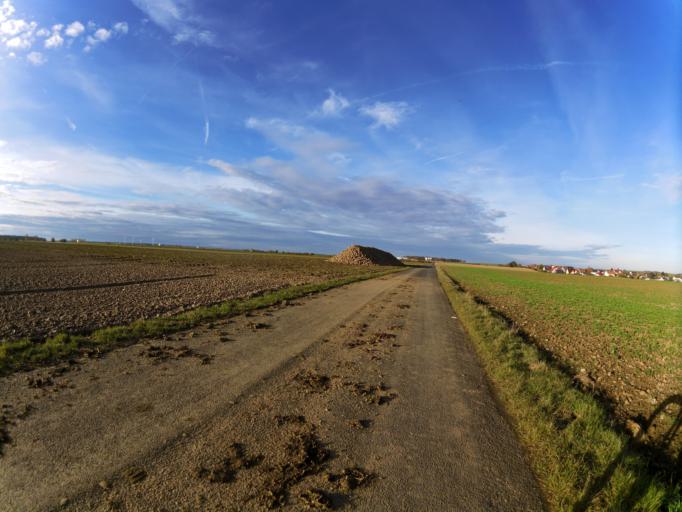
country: DE
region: Bavaria
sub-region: Regierungsbezirk Unterfranken
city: Giebelstadt
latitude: 49.6650
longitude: 9.9515
